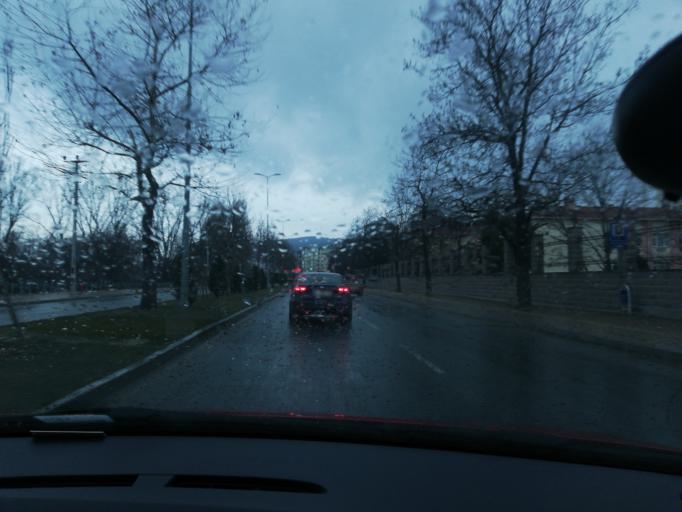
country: TR
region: Kastamonu
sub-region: Cide
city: Kastamonu
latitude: 41.4089
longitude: 33.7888
